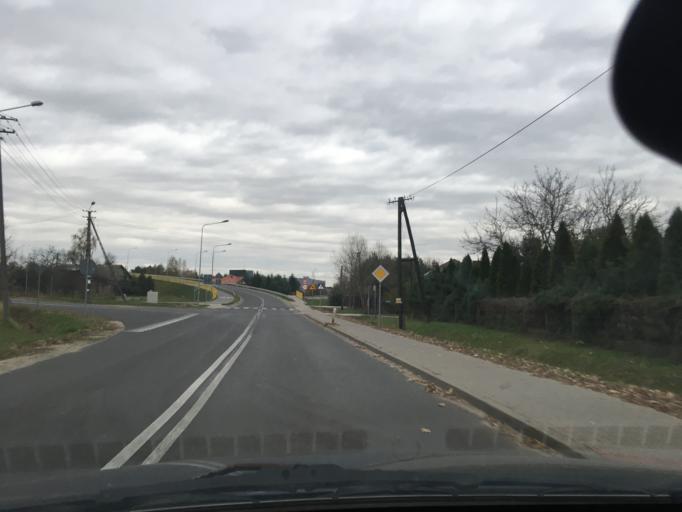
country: PL
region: Lodz Voivodeship
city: Zabia Wola
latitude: 52.0330
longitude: 20.6921
